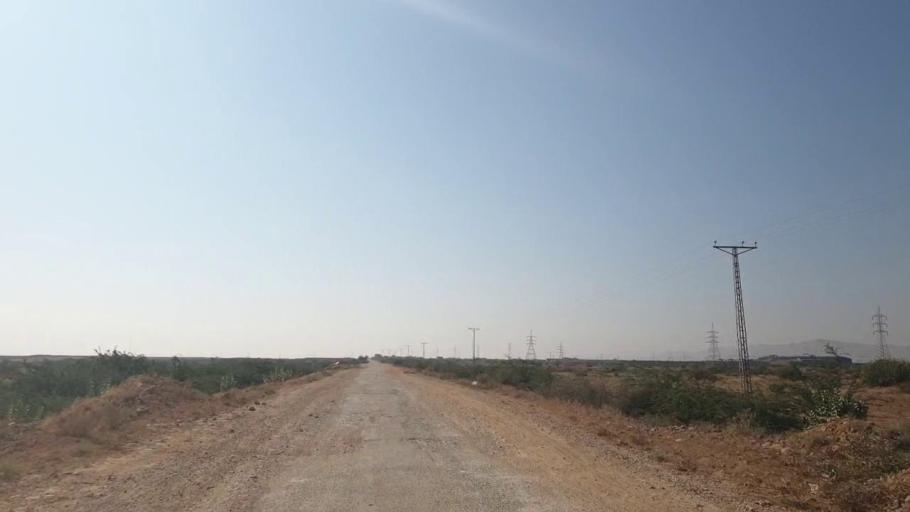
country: PK
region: Sindh
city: Gharo
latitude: 25.1624
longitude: 67.7280
